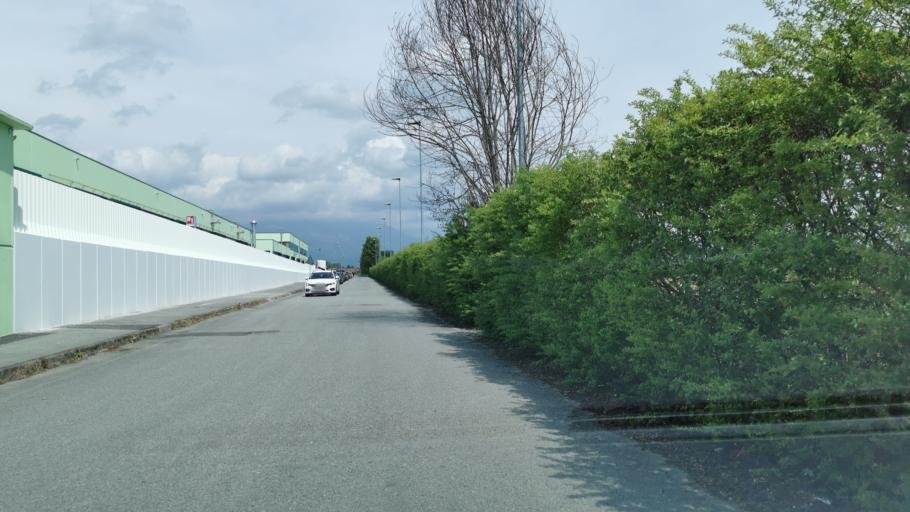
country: IT
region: Piedmont
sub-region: Provincia di Torino
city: Front
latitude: 45.2995
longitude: 7.6704
